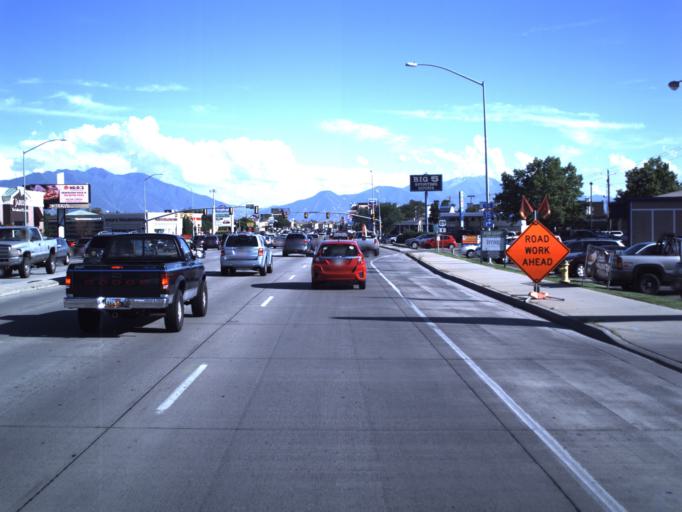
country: US
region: Utah
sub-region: Utah County
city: Orem
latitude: 40.2749
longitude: -111.6854
